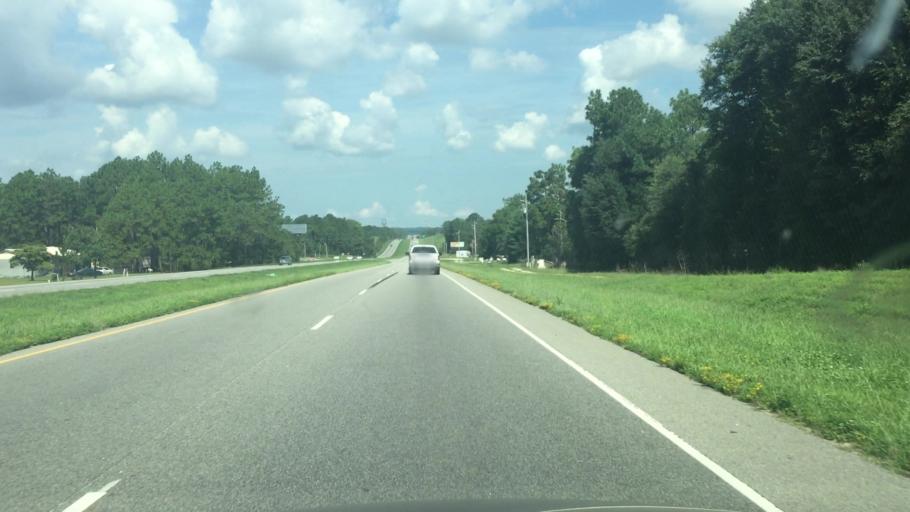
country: US
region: North Carolina
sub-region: Scotland County
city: Laurel Hill
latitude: 34.8426
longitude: -79.6057
